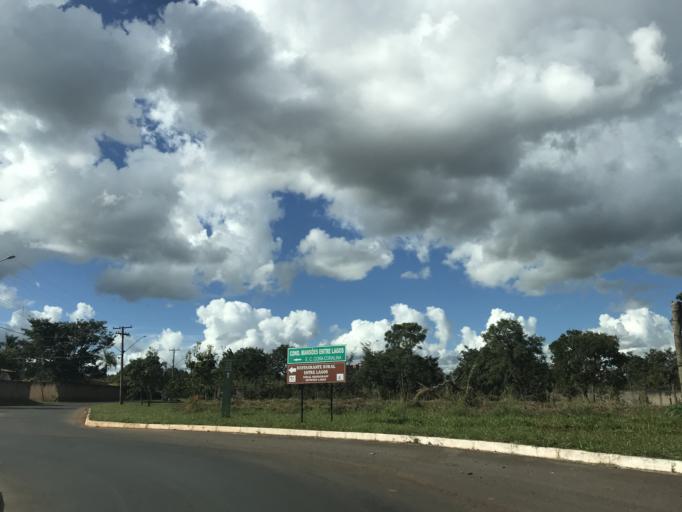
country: BR
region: Federal District
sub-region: Brasilia
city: Brasilia
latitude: -15.7493
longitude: -47.7502
